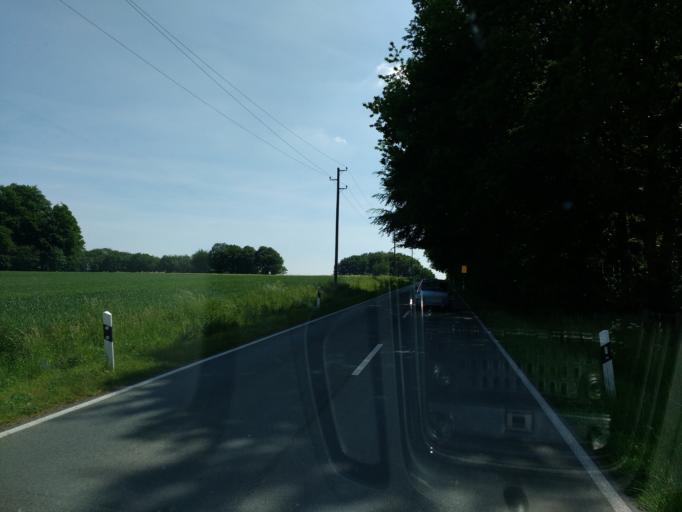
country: DE
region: Lower Saxony
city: Belm
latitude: 52.3189
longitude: 8.1111
